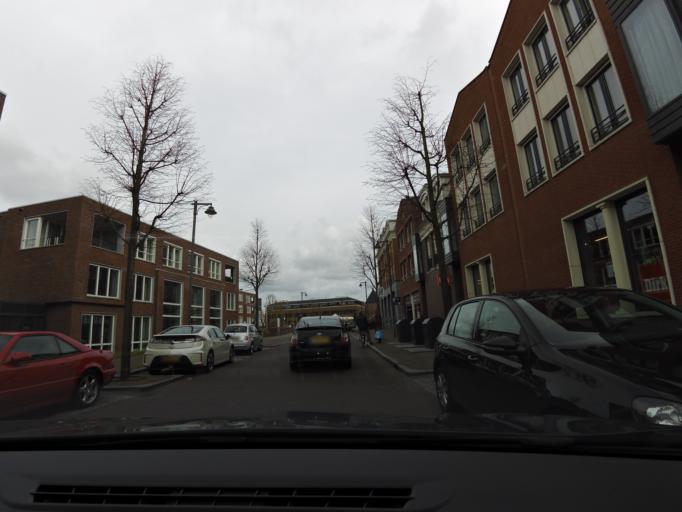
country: NL
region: South Holland
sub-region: Gemeente Noordwijk
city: Noordwijk-Binnen
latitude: 52.2351
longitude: 4.4474
